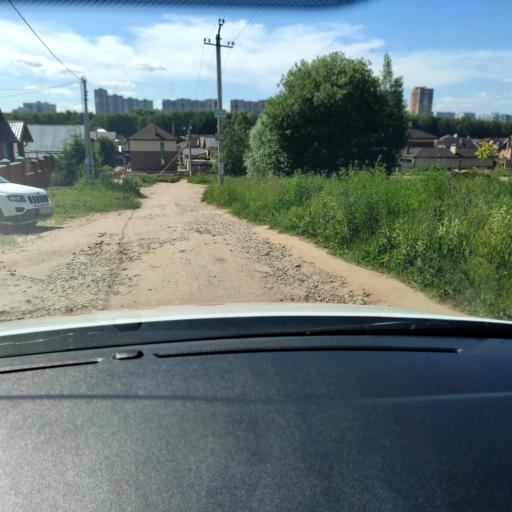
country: RU
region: Tatarstan
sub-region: Gorod Kazan'
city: Kazan
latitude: 55.7777
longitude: 49.2573
